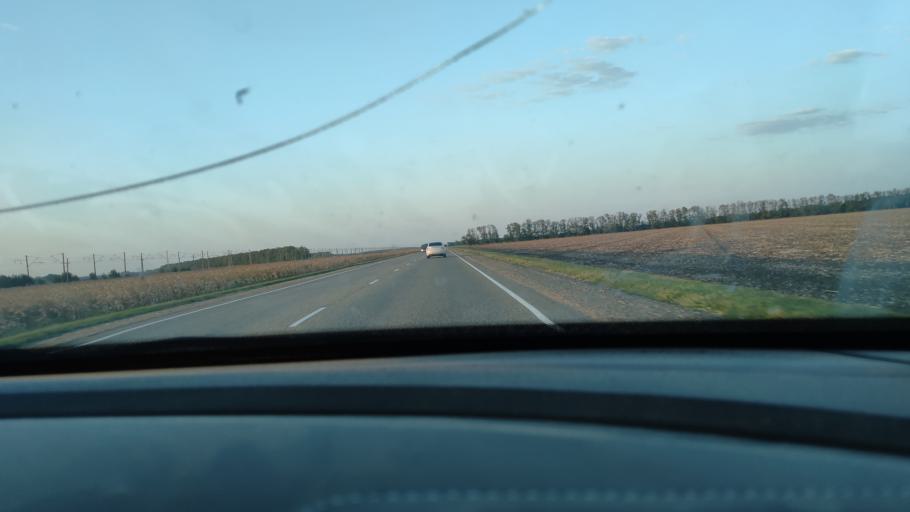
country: RU
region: Krasnodarskiy
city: Novominskaya
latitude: 46.3732
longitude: 38.9772
